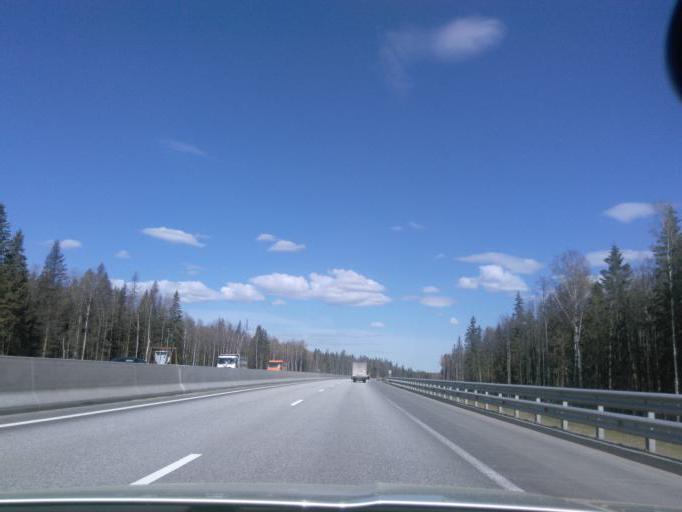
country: RU
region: Moskovskaya
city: Mendeleyevo
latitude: 56.0712
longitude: 37.2201
